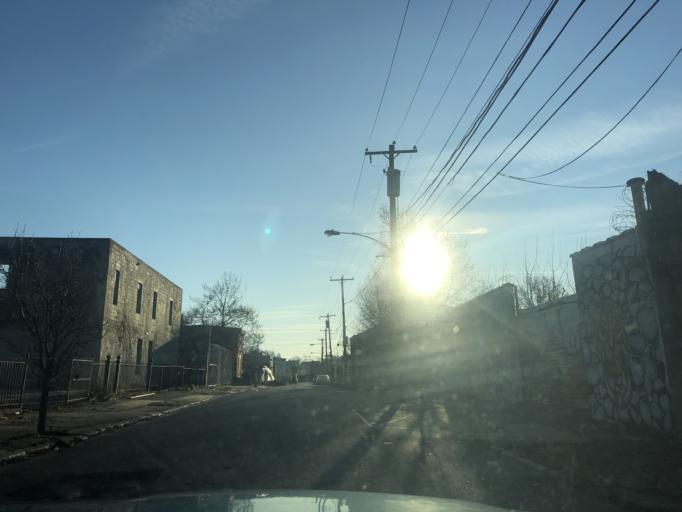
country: US
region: Pennsylvania
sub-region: Delaware County
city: Millbourne
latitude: 39.9759
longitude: -75.2261
